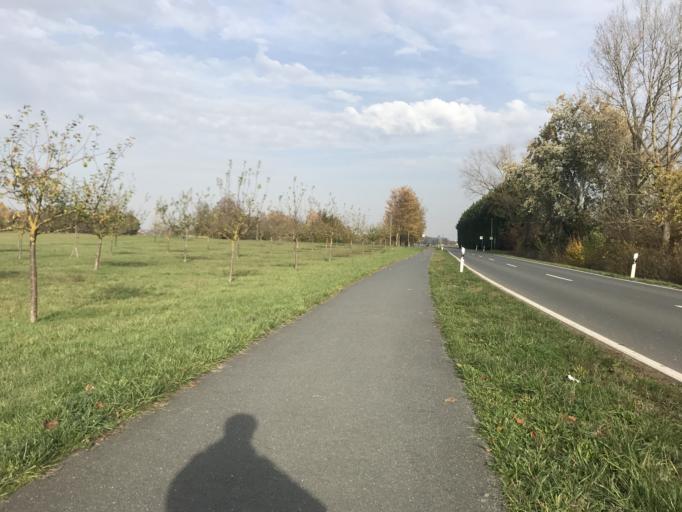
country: DE
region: Hesse
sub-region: Regierungsbezirk Darmstadt
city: Trebur
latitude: 49.9429
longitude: 8.3802
